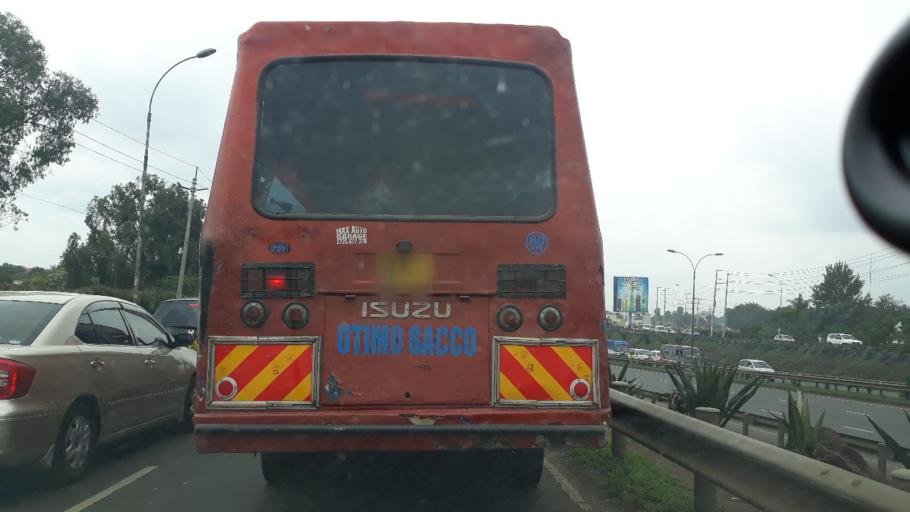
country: KE
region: Nairobi Area
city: Pumwani
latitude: -1.2464
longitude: 36.8651
